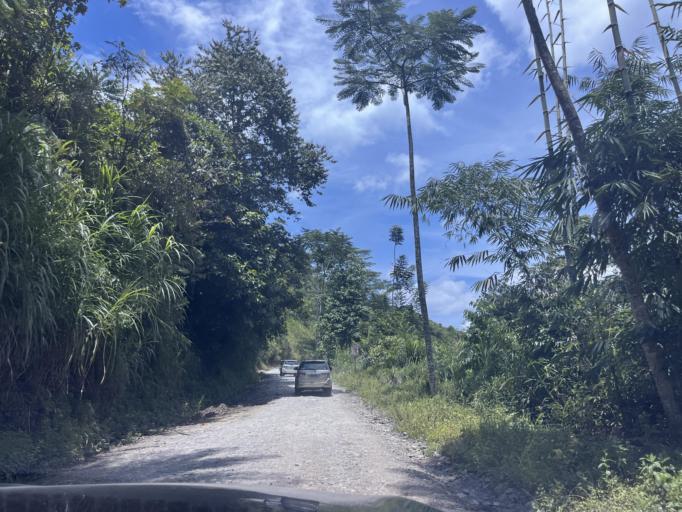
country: PH
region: Northern Mindanao
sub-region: Province of Bukidnon
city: Kisolon
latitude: 8.3116
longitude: 124.9681
